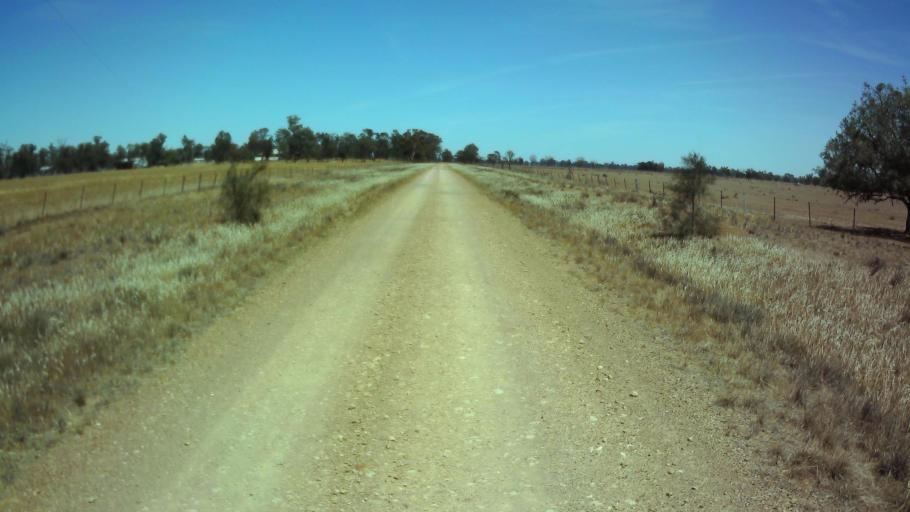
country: AU
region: New South Wales
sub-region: Weddin
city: Grenfell
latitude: -34.0671
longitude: 147.8838
